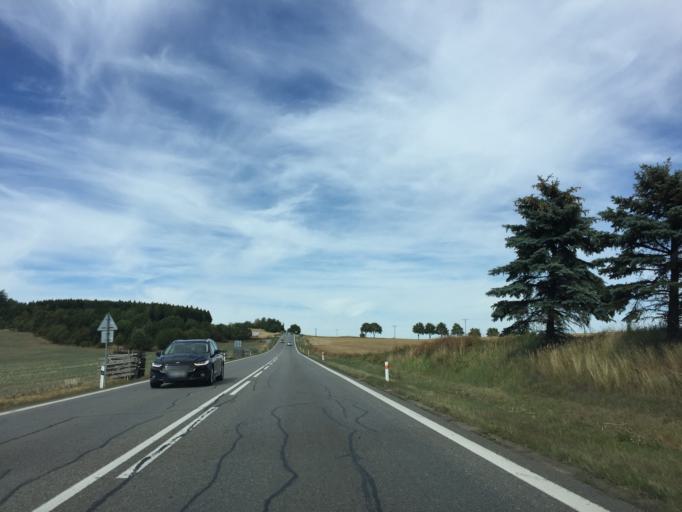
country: CZ
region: Jihocesky
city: Chotoviny
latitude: 49.5485
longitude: 14.6649
